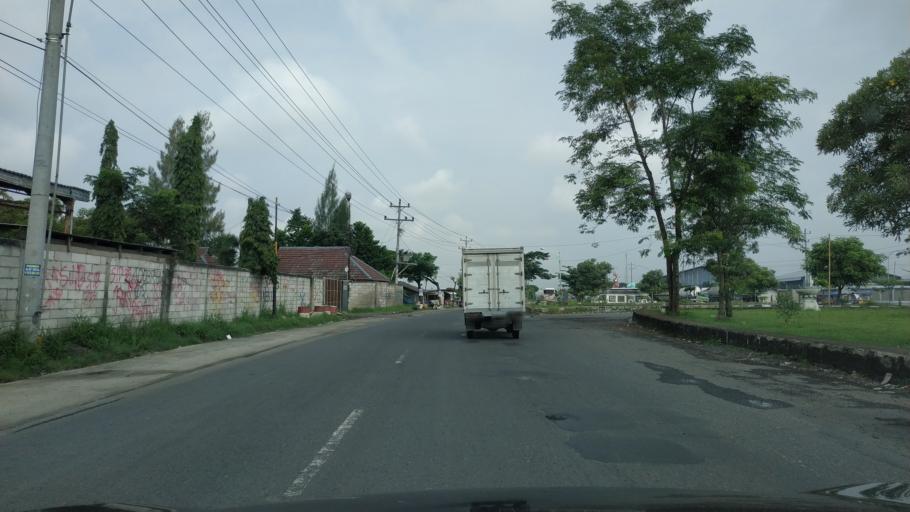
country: ID
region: Central Java
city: Bulakamba
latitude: -6.8724
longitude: 108.9065
